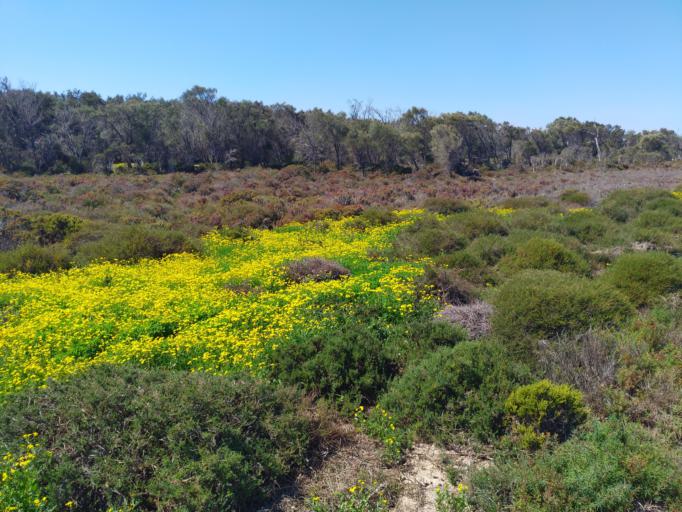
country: AU
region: Western Australia
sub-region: Mandurah
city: Erskine
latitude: -32.5580
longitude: 115.7359
